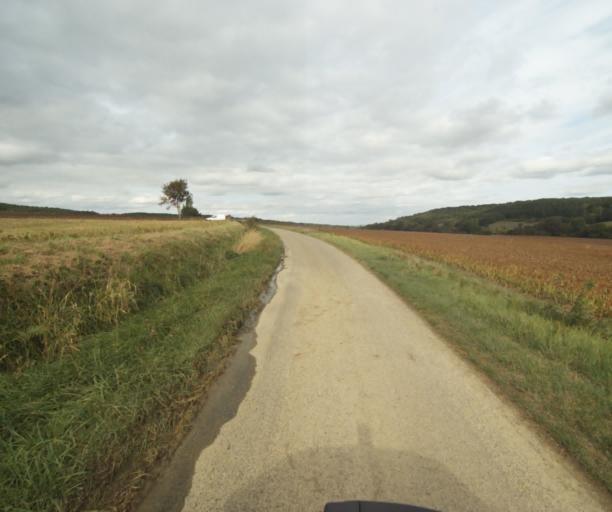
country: FR
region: Midi-Pyrenees
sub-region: Departement du Tarn-et-Garonne
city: Beaumont-de-Lomagne
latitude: 43.8192
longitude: 1.0831
